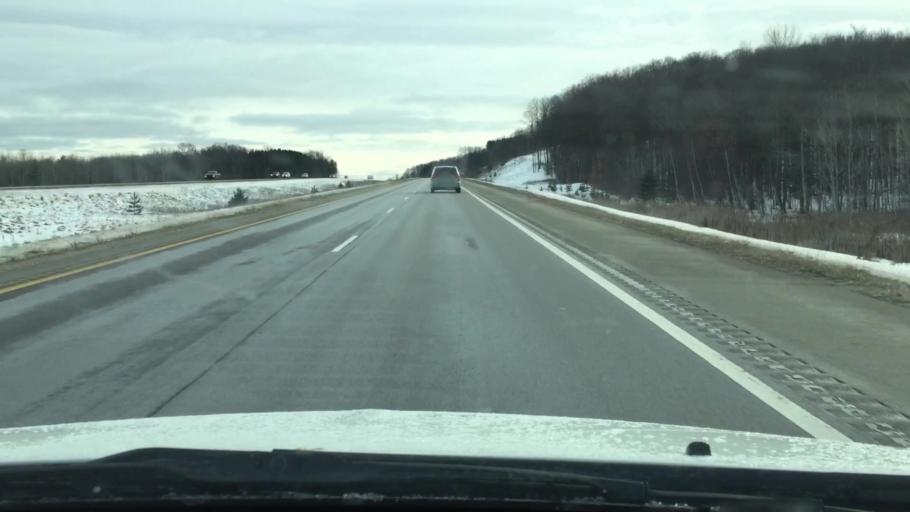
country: US
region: Michigan
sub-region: Wexford County
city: Manton
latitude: 44.4473
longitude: -85.3955
